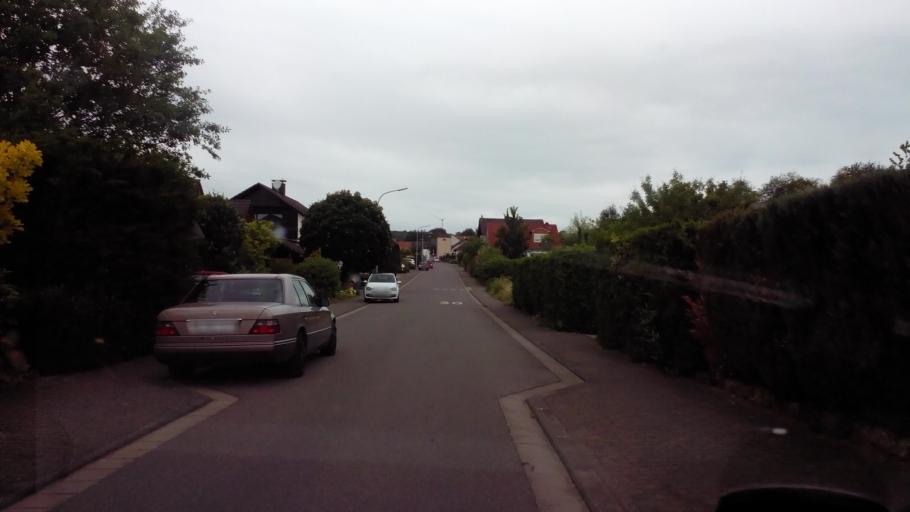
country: DE
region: Saarland
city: Lebach
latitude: 49.4162
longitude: 6.9045
